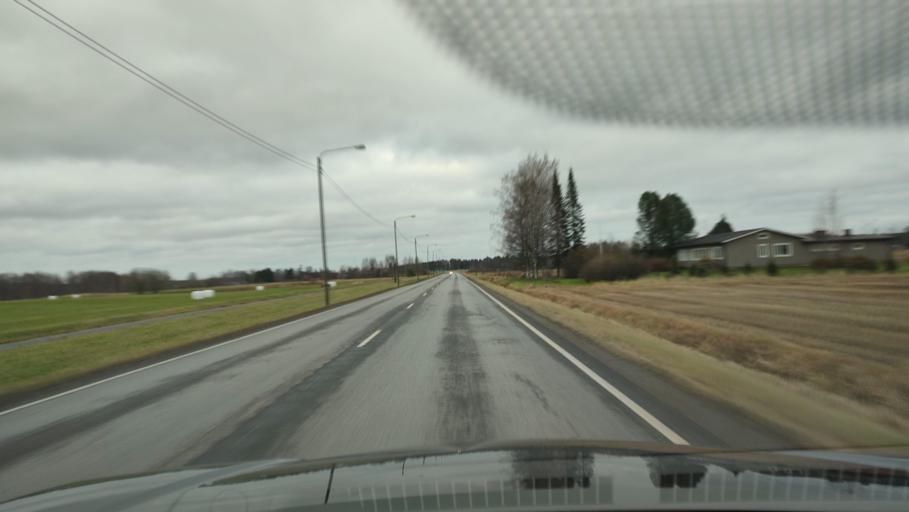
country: FI
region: Southern Ostrobothnia
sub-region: Seinaejoki
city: Kurikka
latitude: 62.6074
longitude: 22.4198
